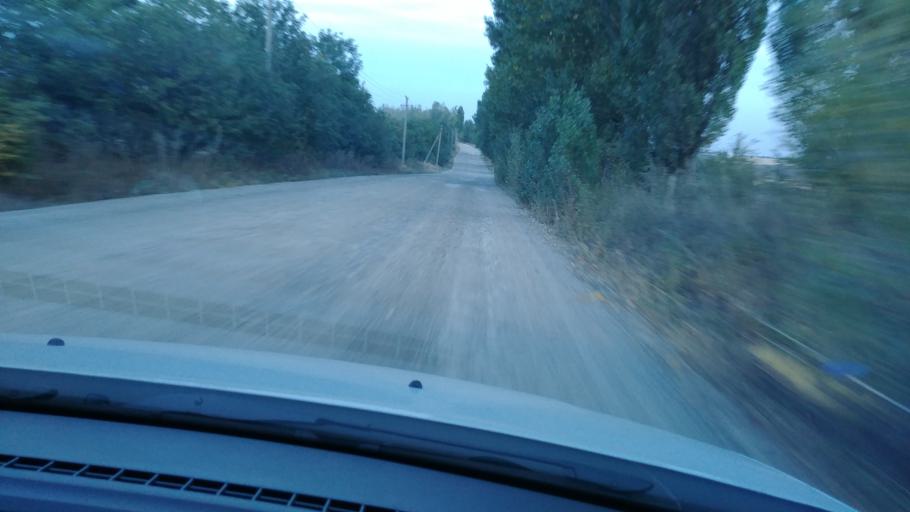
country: MD
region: Rezina
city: Saharna
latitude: 47.6783
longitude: 28.9227
